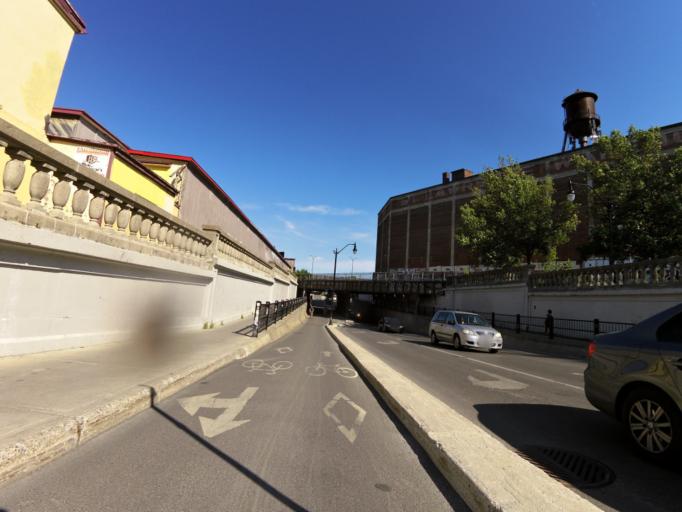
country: CA
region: Quebec
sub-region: Montreal
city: Montreal
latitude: 45.5288
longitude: -73.6053
